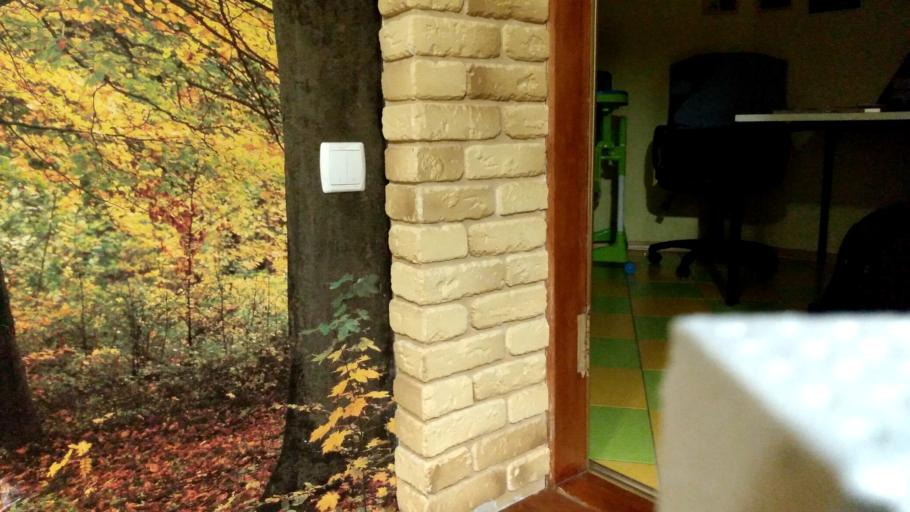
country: RU
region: Arkhangelskaya
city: Kargopol'
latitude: 61.4664
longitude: 37.7923
